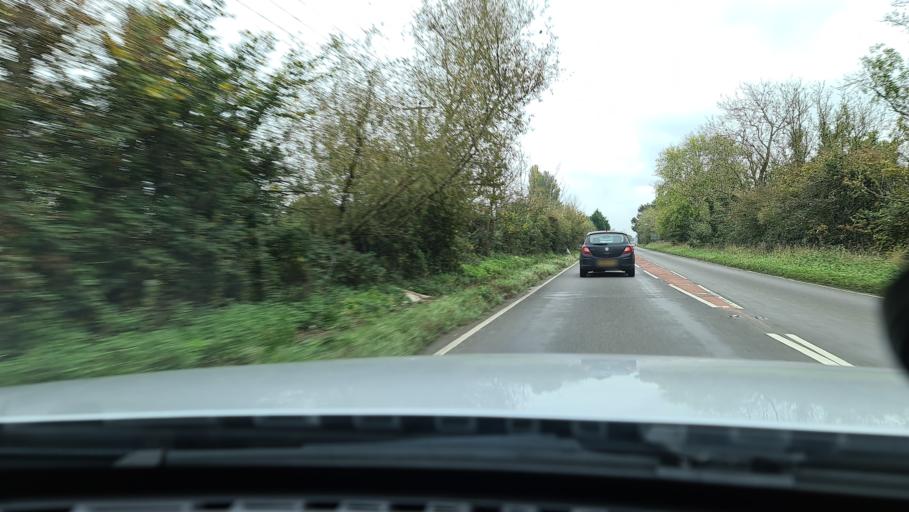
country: GB
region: England
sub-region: Buckinghamshire
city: Steeple Claydon
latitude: 51.8735
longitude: -1.0567
